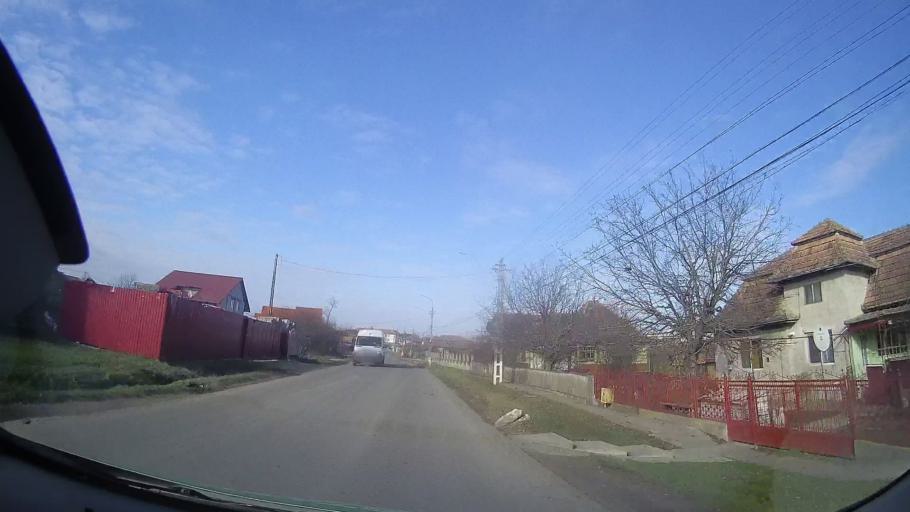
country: RO
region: Mures
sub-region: Comuna Valea Larga
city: Valea Larga
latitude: 46.6185
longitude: 24.0797
